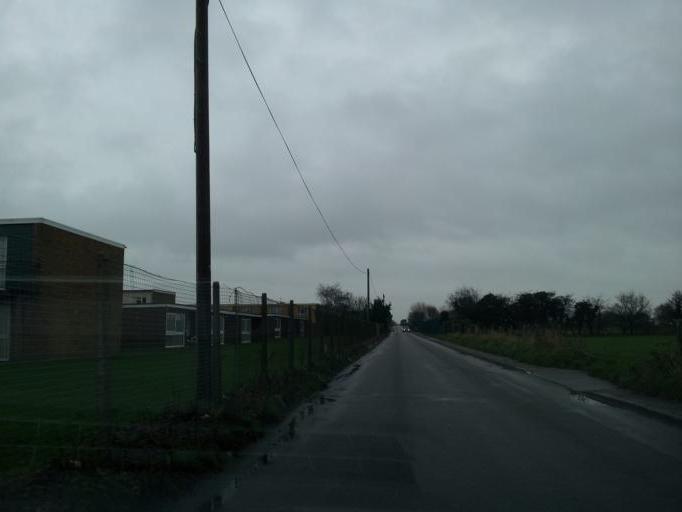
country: GB
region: England
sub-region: Norfolk
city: Hemsby
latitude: 52.6917
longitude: 1.6982
